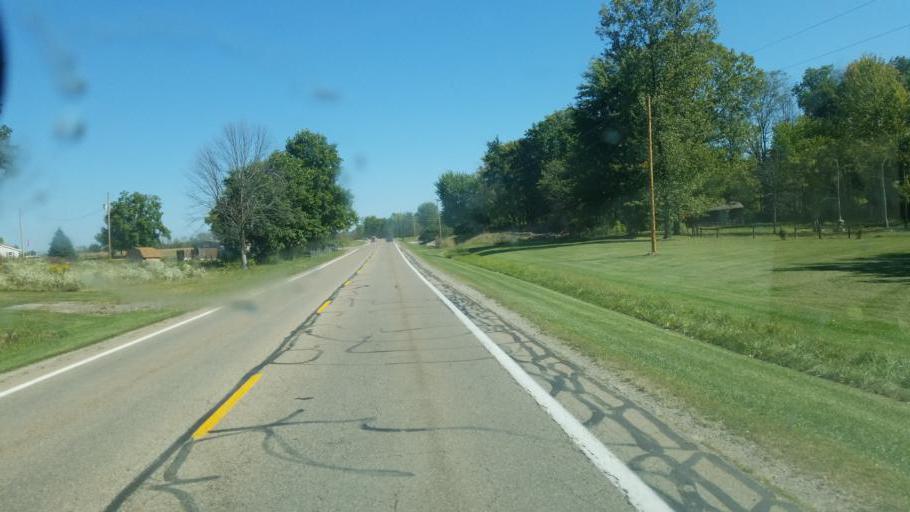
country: US
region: Ohio
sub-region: Crawford County
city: Galion
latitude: 40.6602
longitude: -82.8722
